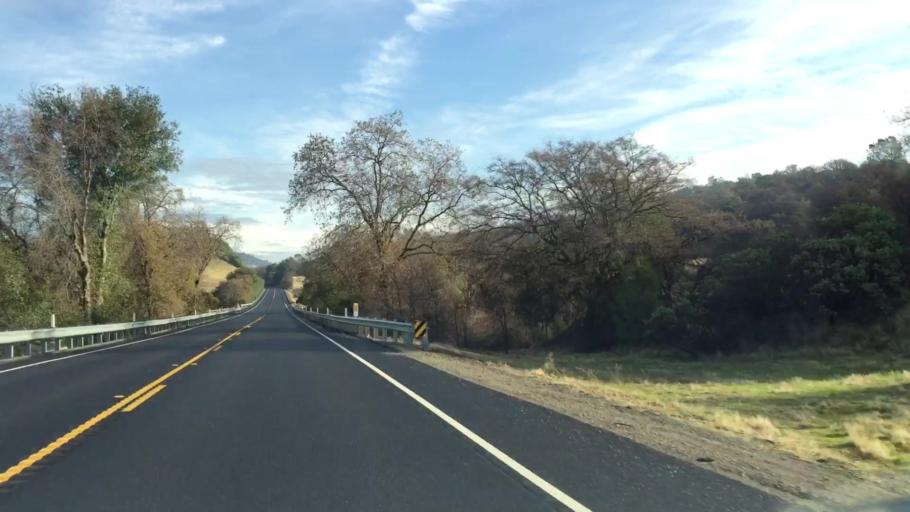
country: US
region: California
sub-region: Butte County
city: Oroville
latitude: 39.6367
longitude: -121.5794
